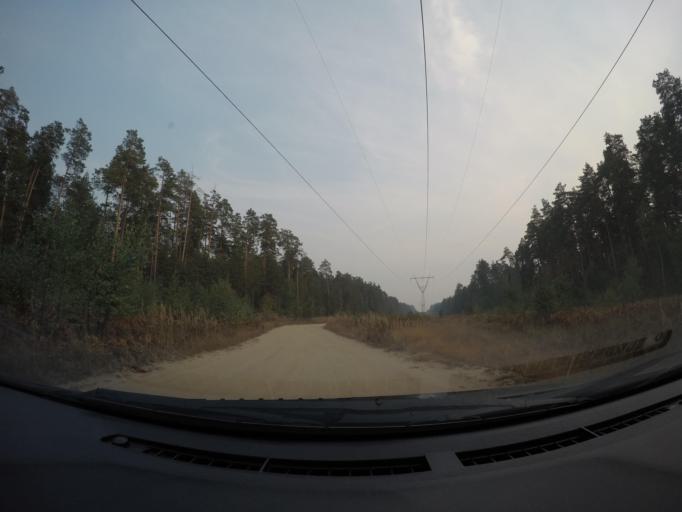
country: RU
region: Moskovskaya
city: Imeni Tsyurupy
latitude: 55.4994
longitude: 38.6878
